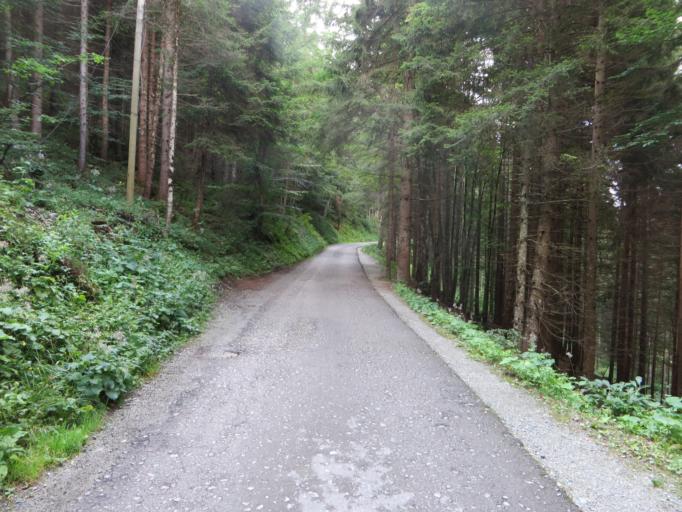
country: IT
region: Trentino-Alto Adige
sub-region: Provincia di Trento
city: Carisolo
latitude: 46.2187
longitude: 10.8286
